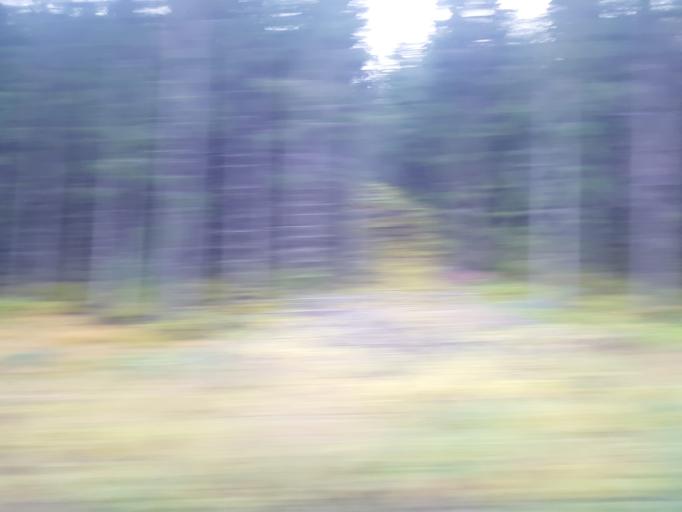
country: NO
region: Oppland
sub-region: Dovre
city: Dovre
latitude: 61.9258
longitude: 9.3285
